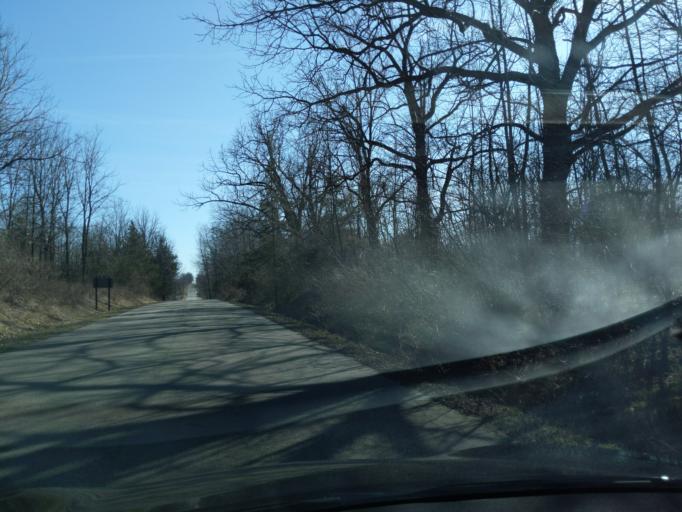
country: US
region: Michigan
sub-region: Ionia County
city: Saranac
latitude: 42.9341
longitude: -85.1341
